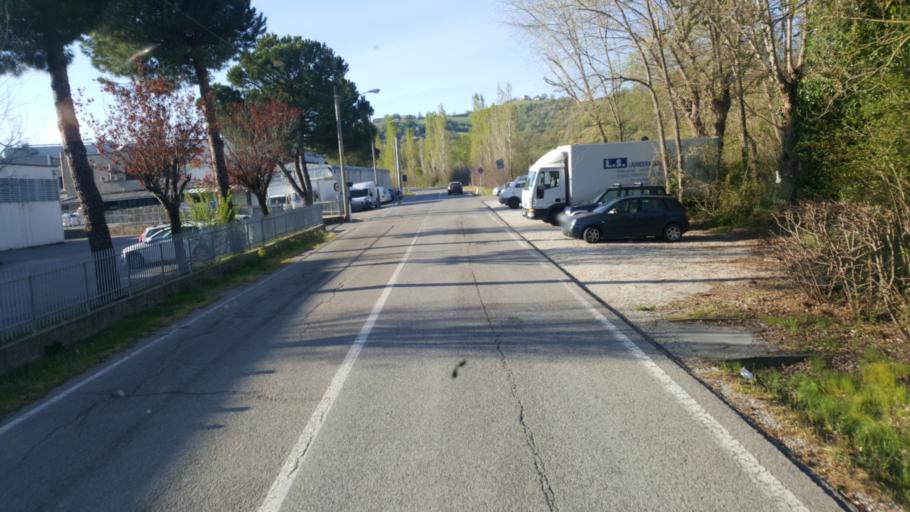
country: SM
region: Acquaviva
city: Acquaviva
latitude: 43.9448
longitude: 12.4056
